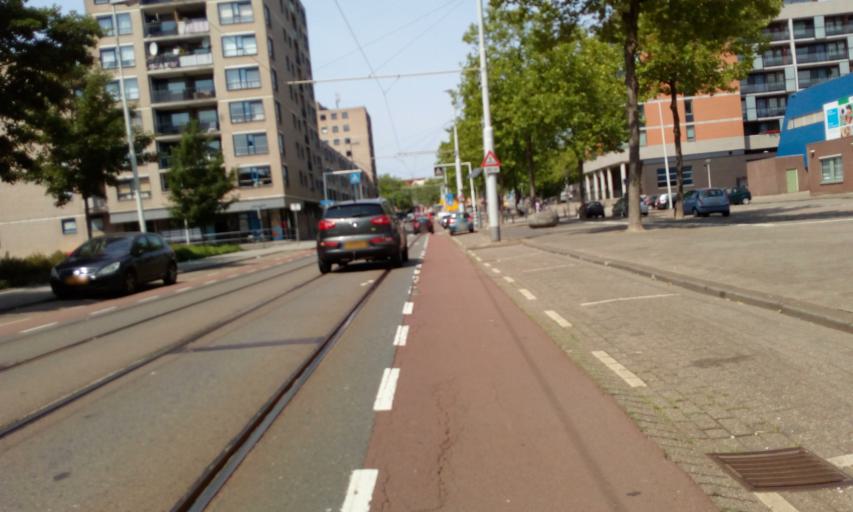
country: NL
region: South Holland
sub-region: Gemeente Rotterdam
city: Rotterdam
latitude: 51.9331
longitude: 4.4914
